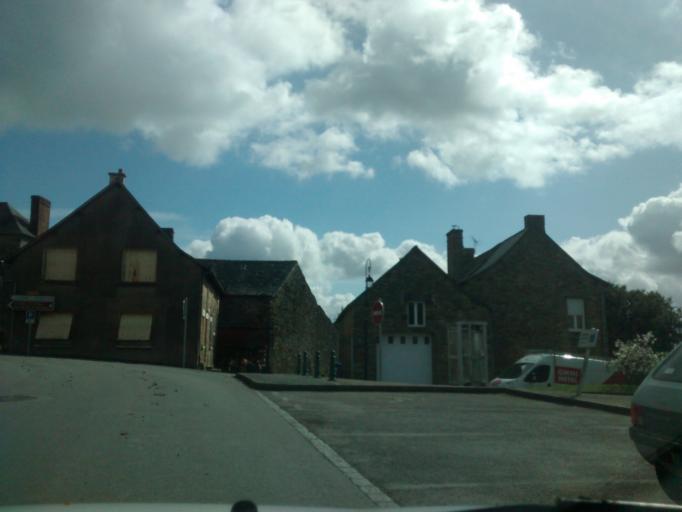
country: FR
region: Brittany
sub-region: Departement d'Ille-et-Vilaine
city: Livre-sur-Changeon
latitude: 48.1930
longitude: -1.3692
